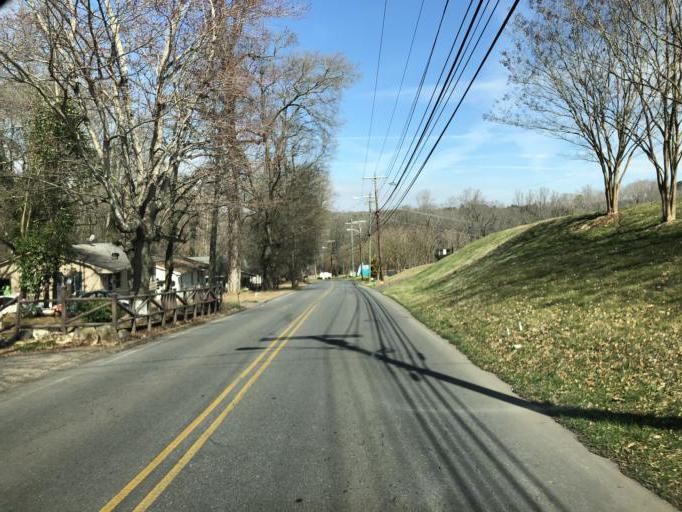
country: US
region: North Carolina
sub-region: Cleveland County
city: Shelby
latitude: 35.3049
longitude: -81.5378
